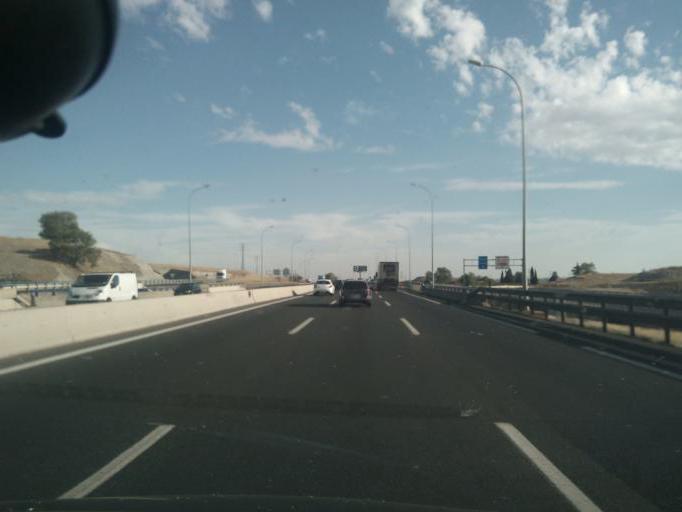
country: ES
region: Madrid
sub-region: Provincia de Madrid
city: Pinto
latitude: 40.2324
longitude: -3.6895
